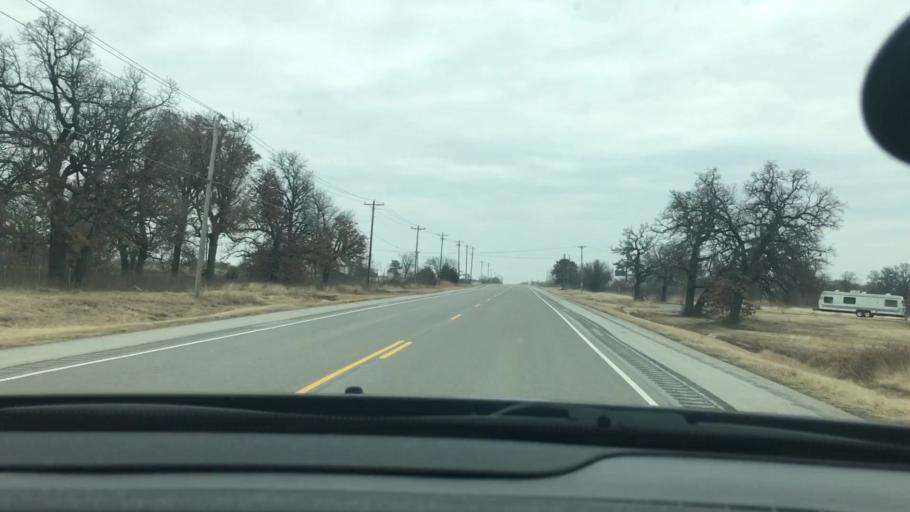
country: US
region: Oklahoma
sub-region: Carter County
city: Healdton
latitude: 34.4004
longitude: -97.5061
